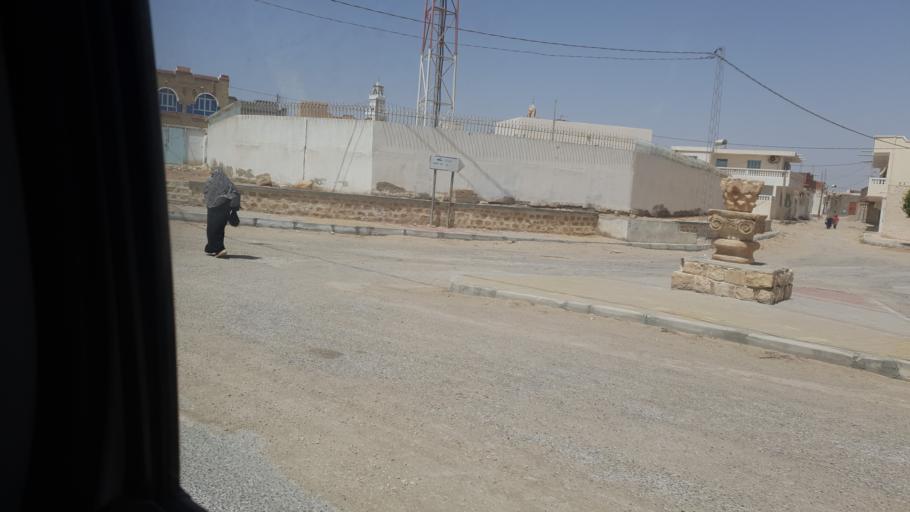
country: TN
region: Qibili
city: Kebili
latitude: 33.7148
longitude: 8.9227
